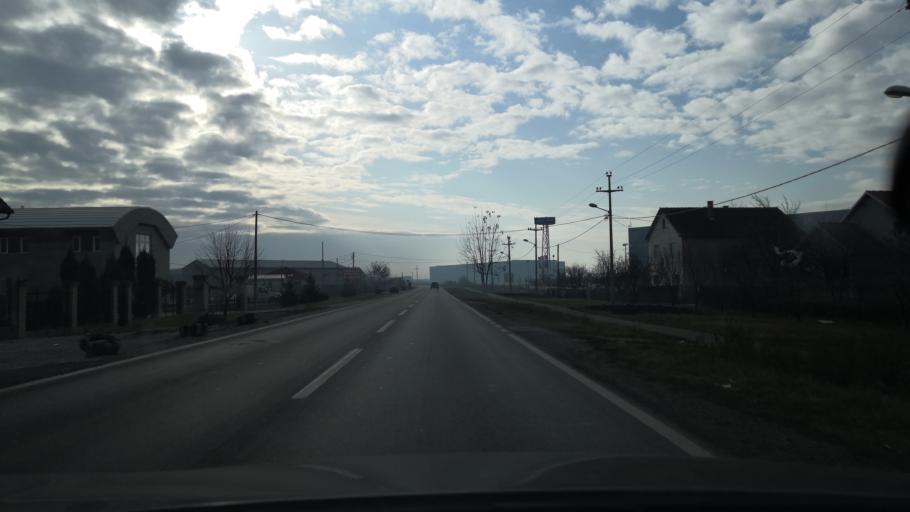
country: RS
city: Ugrinovci
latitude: 44.8563
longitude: 20.2052
